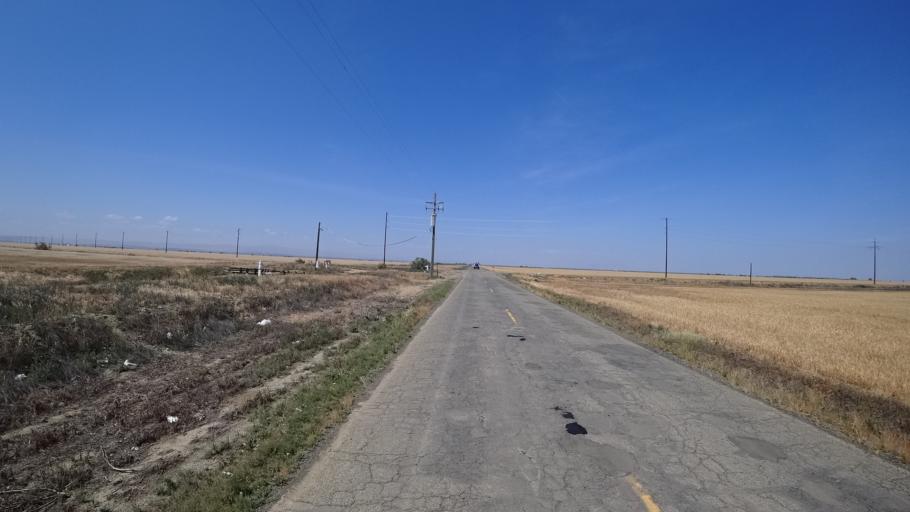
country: US
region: California
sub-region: Kings County
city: Stratford
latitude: 36.1378
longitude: -119.9045
